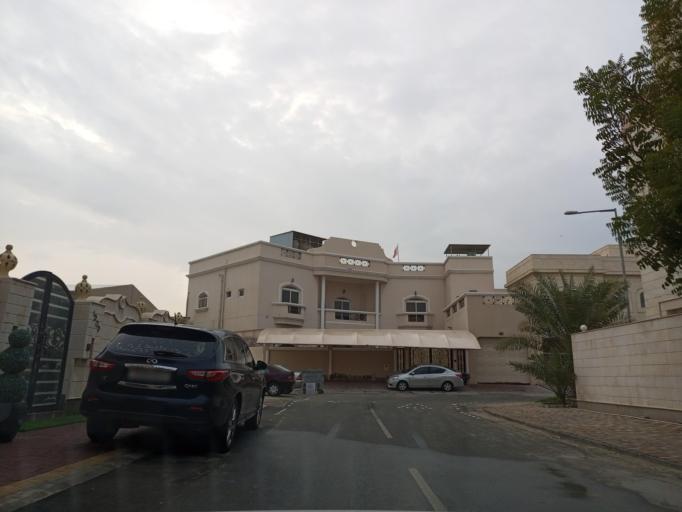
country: BH
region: Muharraq
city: Al Hadd
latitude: 26.2425
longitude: 50.6425
